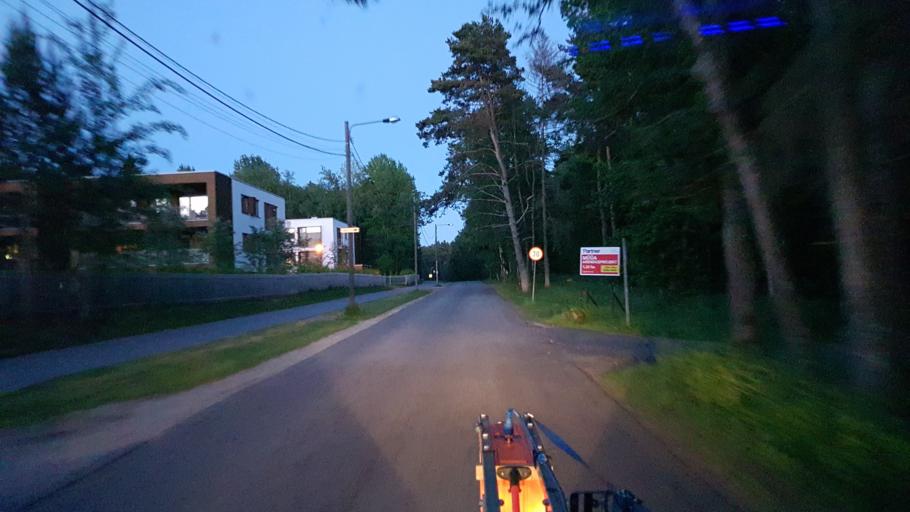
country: EE
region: Harju
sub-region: Harku vald
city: Tabasalu
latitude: 59.4504
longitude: 24.5868
